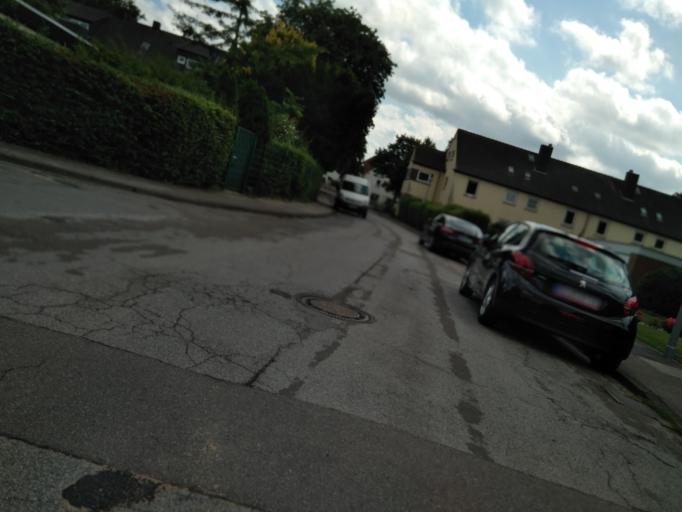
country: DE
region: North Rhine-Westphalia
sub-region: Regierungsbezirk Munster
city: Gladbeck
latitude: 51.5945
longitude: 6.9798
